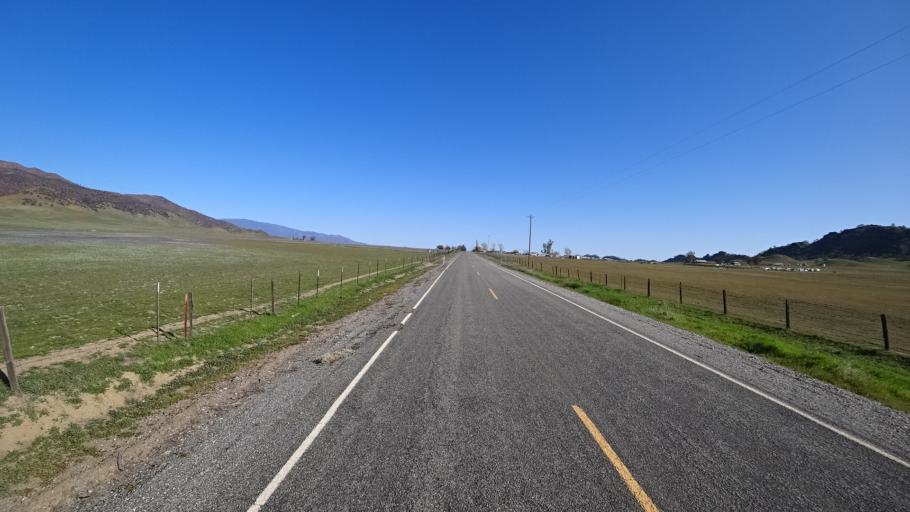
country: US
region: California
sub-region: Tehama County
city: Rancho Tehama Reserve
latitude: 39.7223
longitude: -122.5497
